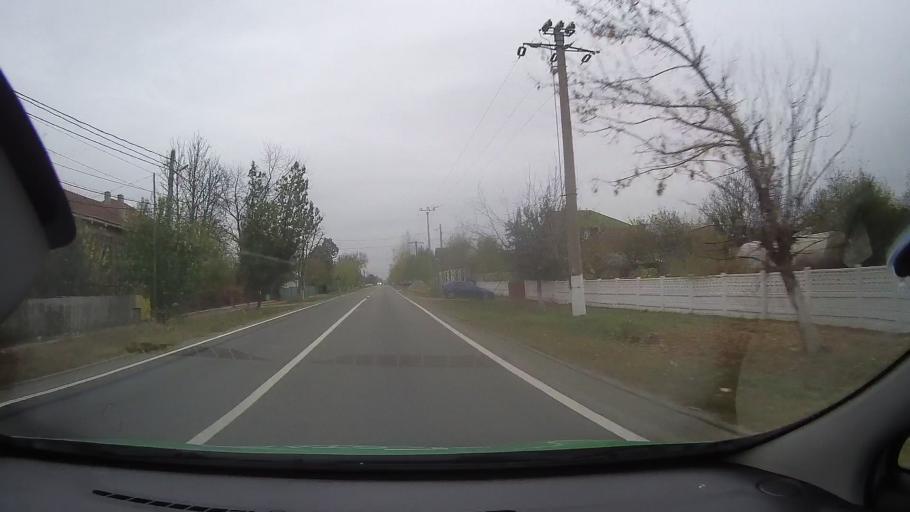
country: RO
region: Ialomita
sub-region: Comuna Slobozia
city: Slobozia
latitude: 44.6022
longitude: 27.3877
